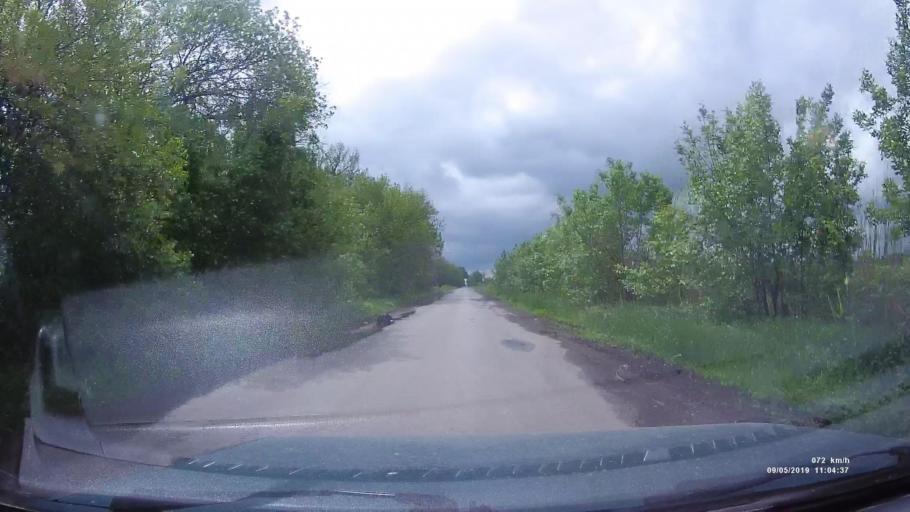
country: RU
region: Krasnodarskiy
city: Kanelovskaya
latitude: 46.8149
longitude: 39.2099
